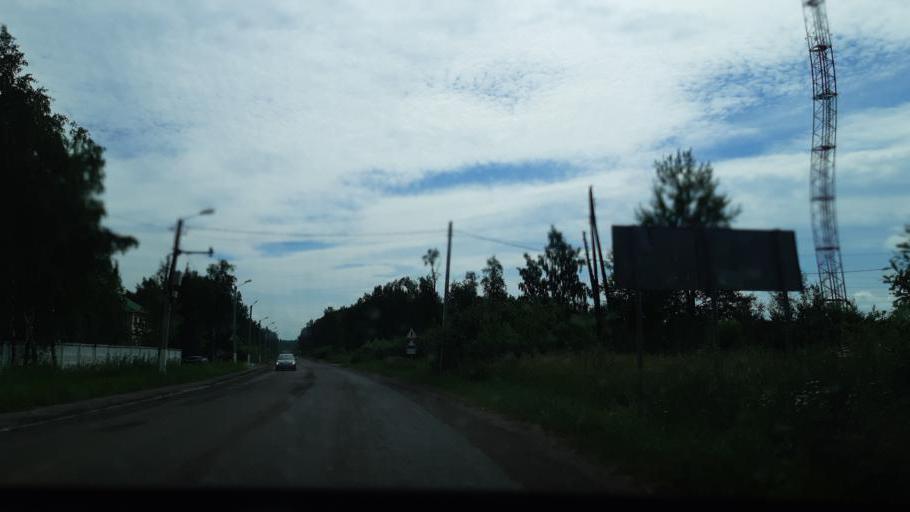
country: RU
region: Moskovskaya
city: Vereya
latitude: 55.3001
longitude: 36.0914
